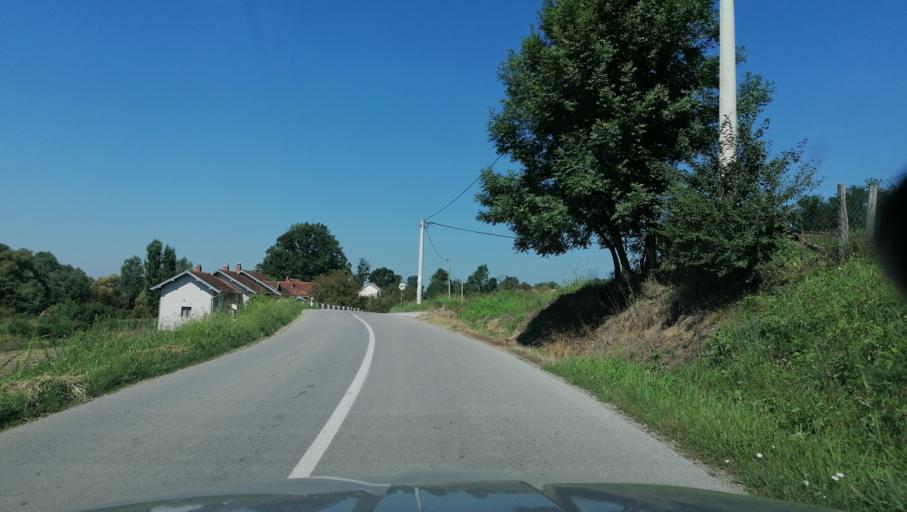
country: RS
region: Central Serbia
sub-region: Raski Okrug
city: Vrnjacka Banja
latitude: 43.6945
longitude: 20.8618
